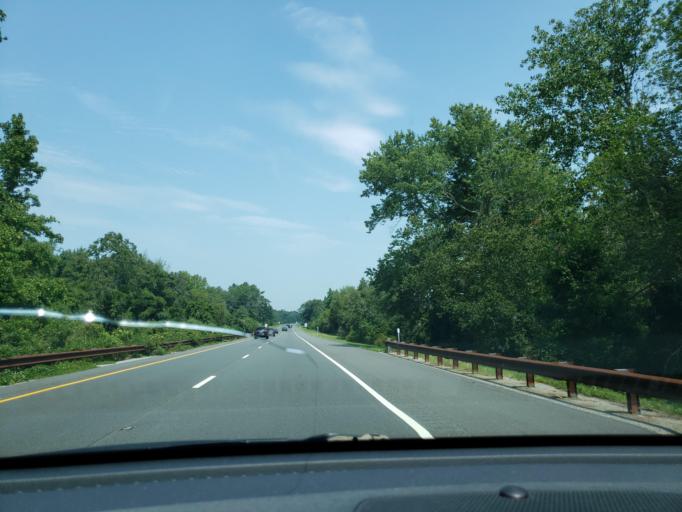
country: US
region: New Jersey
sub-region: Cape May County
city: Sea Isle City
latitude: 39.2041
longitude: -74.6983
